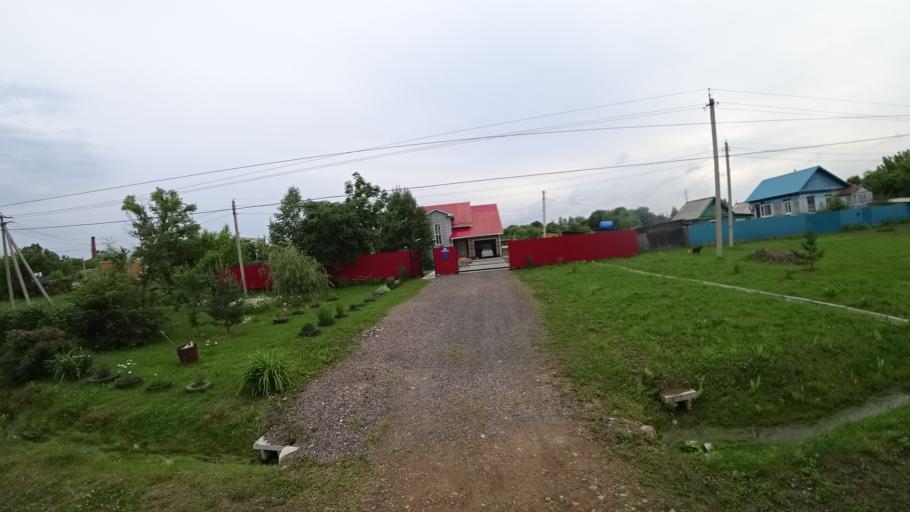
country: RU
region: Primorskiy
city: Novosysoyevka
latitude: 44.2312
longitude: 133.3659
